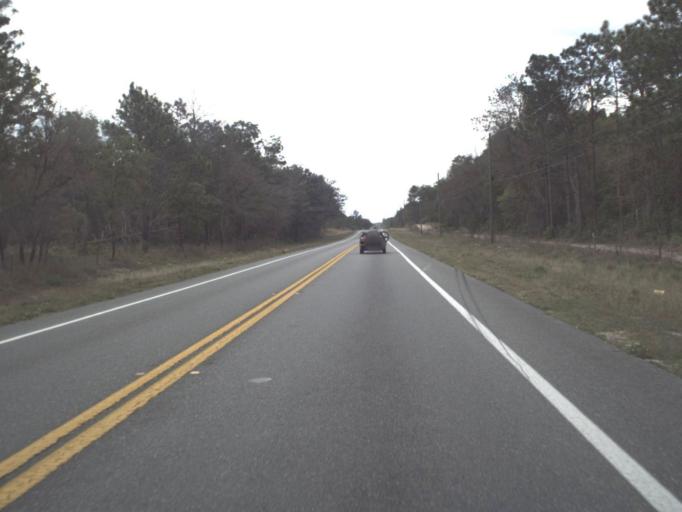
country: US
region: Florida
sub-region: Marion County
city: Ocala
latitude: 29.2517
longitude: -82.0657
